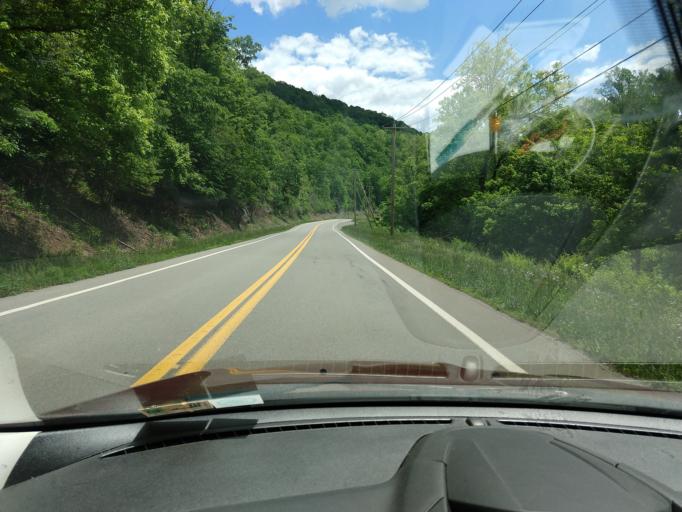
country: US
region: West Virginia
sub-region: Gilmer County
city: Glenville
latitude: 38.8896
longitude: -80.7237
